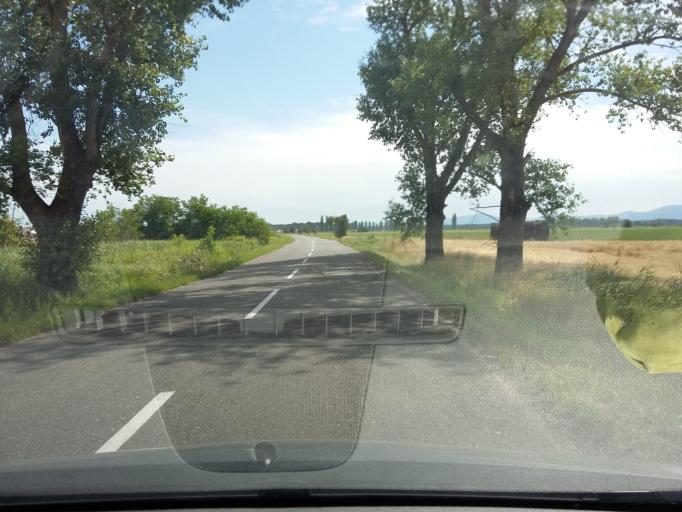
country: SK
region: Bratislavsky
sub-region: Okres Malacky
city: Malacky
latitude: 48.4970
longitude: 16.9785
